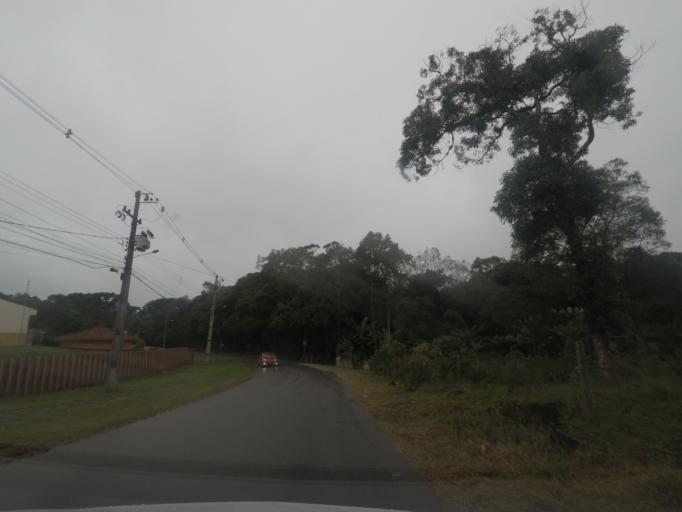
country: BR
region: Parana
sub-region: Colombo
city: Colombo
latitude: -25.3081
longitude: -49.1434
